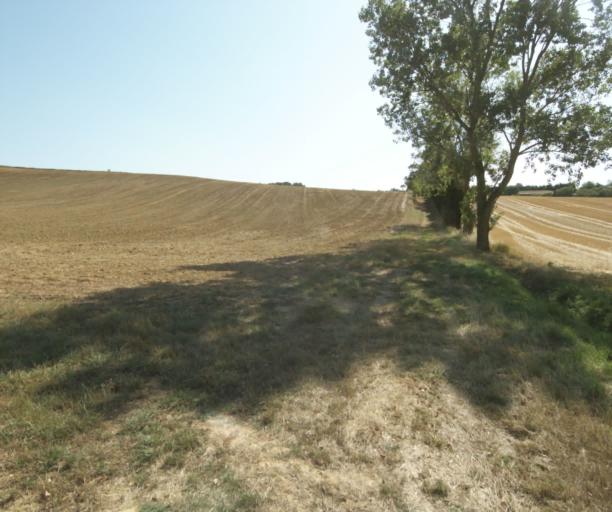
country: FR
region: Midi-Pyrenees
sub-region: Departement de la Haute-Garonne
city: Saint-Felix-Lauragais
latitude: 43.4352
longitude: 1.8496
